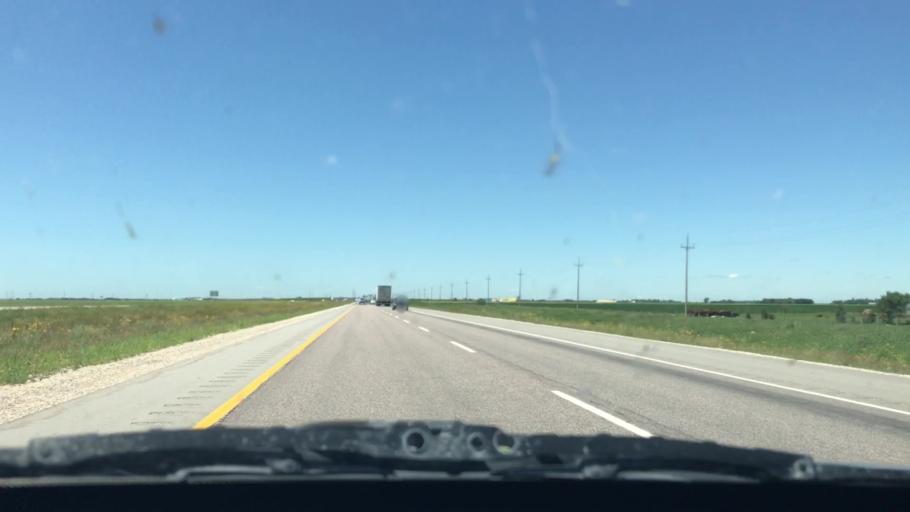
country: CA
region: Manitoba
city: Steinbach
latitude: 49.6908
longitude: -96.6199
